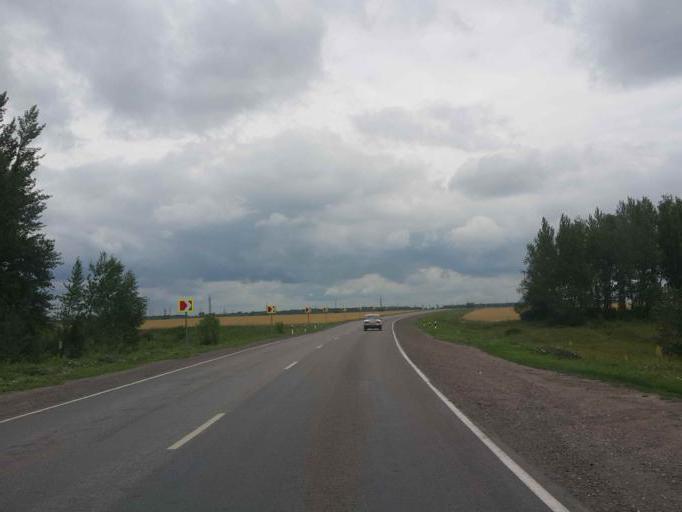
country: RU
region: Tambov
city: Komsomolets
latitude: 52.7492
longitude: 41.2948
